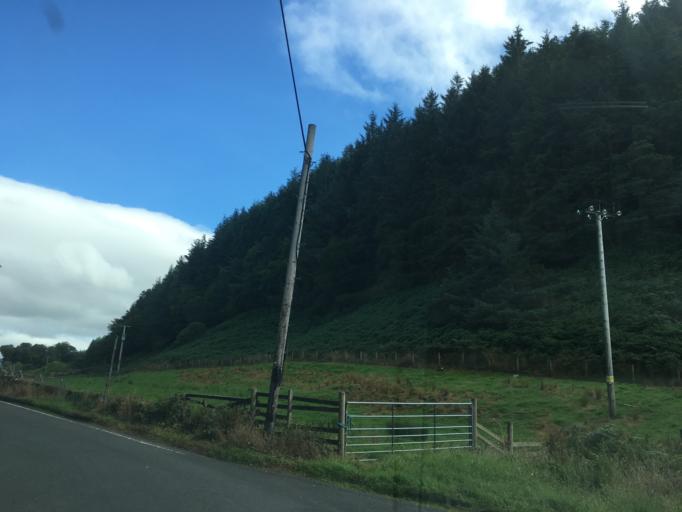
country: GB
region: Scotland
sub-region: Argyll and Bute
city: Ardrishaig
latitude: 56.0852
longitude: -5.5598
